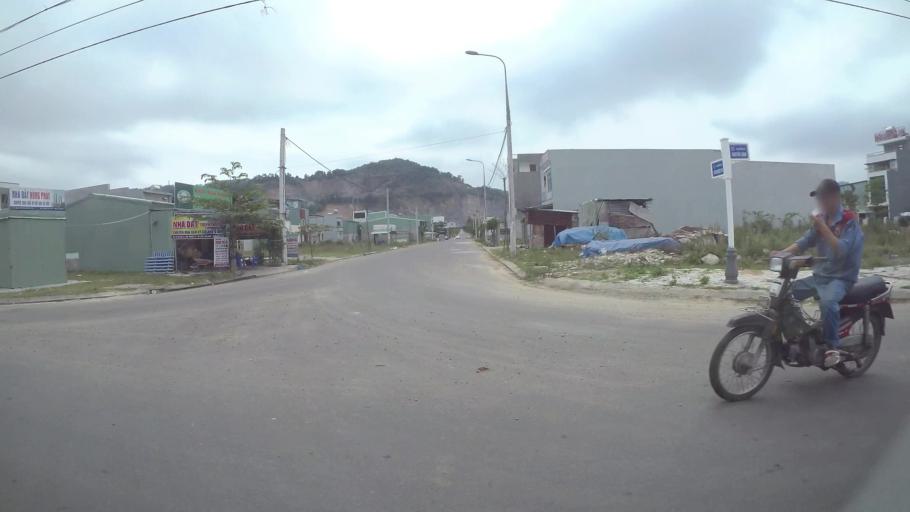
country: VN
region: Da Nang
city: Lien Chieu
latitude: 16.0462
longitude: 108.1695
